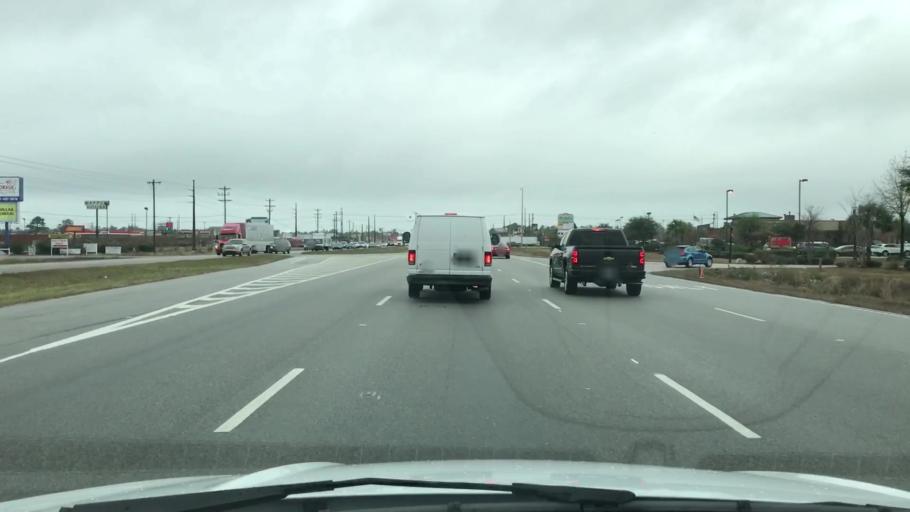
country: US
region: South Carolina
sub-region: Horry County
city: Forestbrook
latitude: 33.7554
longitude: -78.9649
